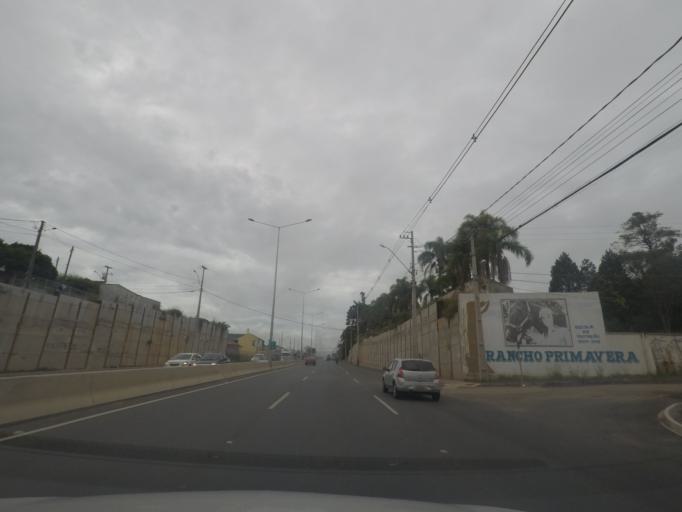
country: BR
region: Parana
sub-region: Piraquara
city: Piraquara
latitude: -25.4560
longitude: -49.1059
